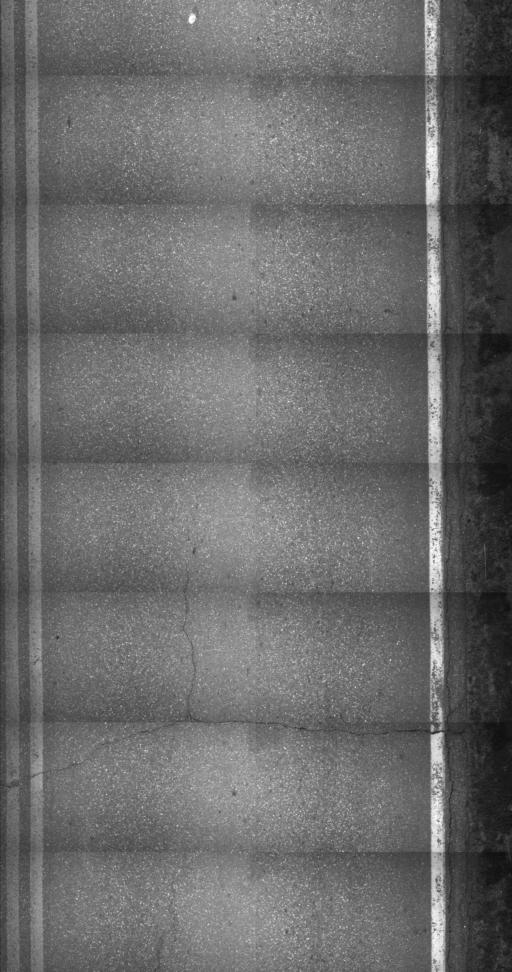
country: US
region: Vermont
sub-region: Orleans County
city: Newport
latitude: 44.9313
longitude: -72.0643
